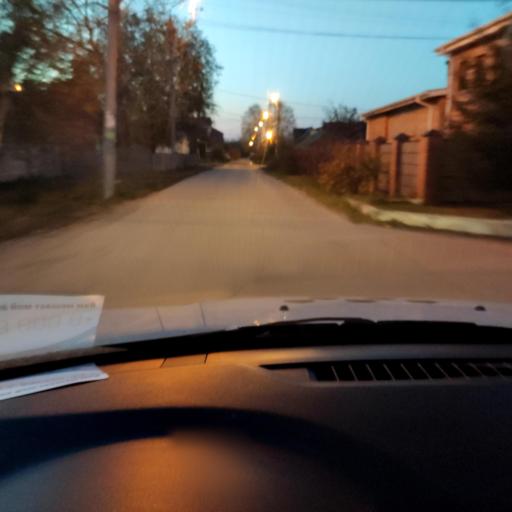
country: RU
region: Samara
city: Tol'yatti
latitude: 53.5352
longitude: 49.4031
